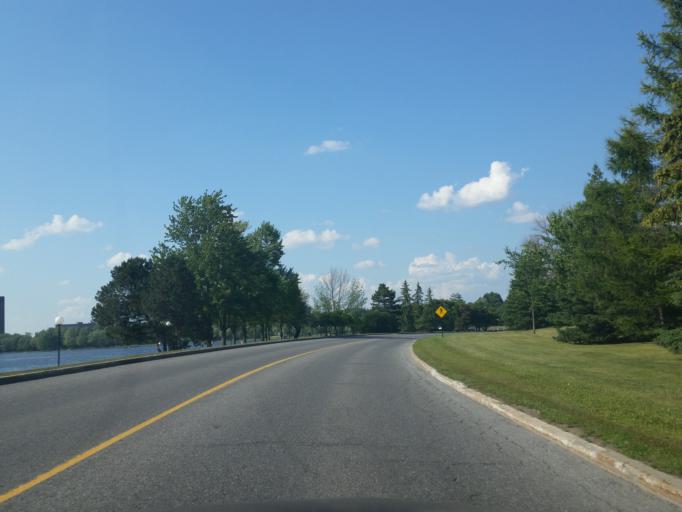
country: CA
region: Ontario
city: Ottawa
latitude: 45.3899
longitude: -75.7003
